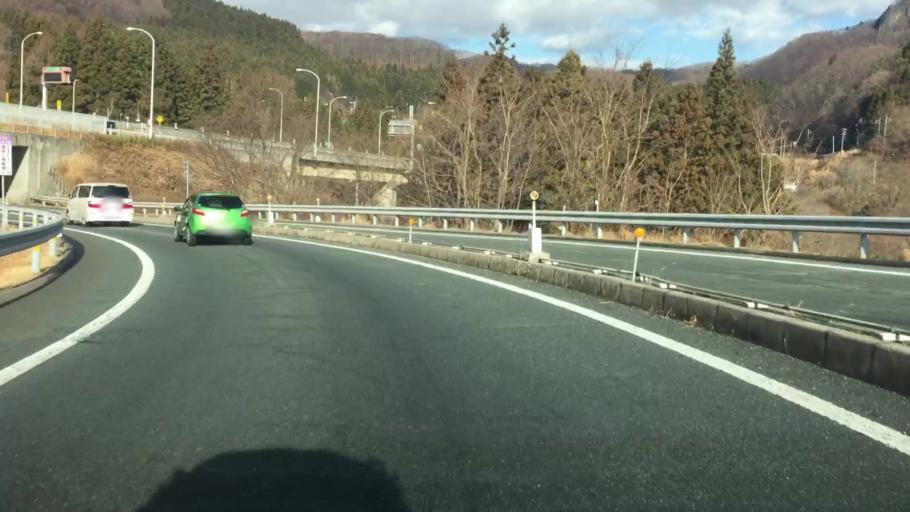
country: JP
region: Nagano
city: Saku
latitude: 36.2936
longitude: 138.6727
